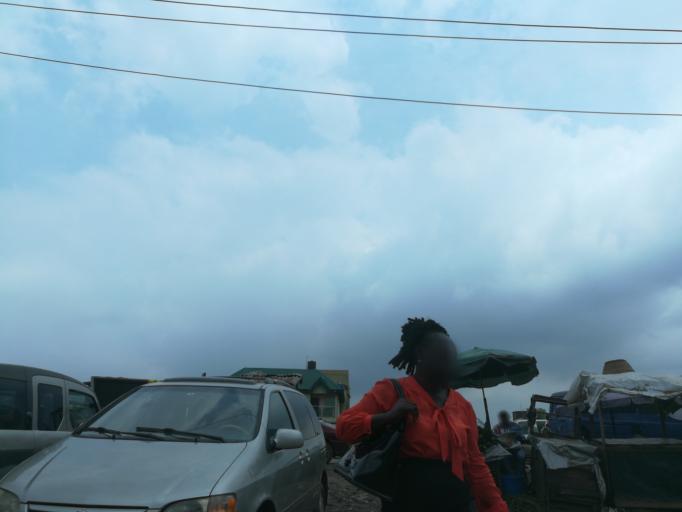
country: NG
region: Lagos
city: Agege
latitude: 6.6197
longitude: 3.3258
